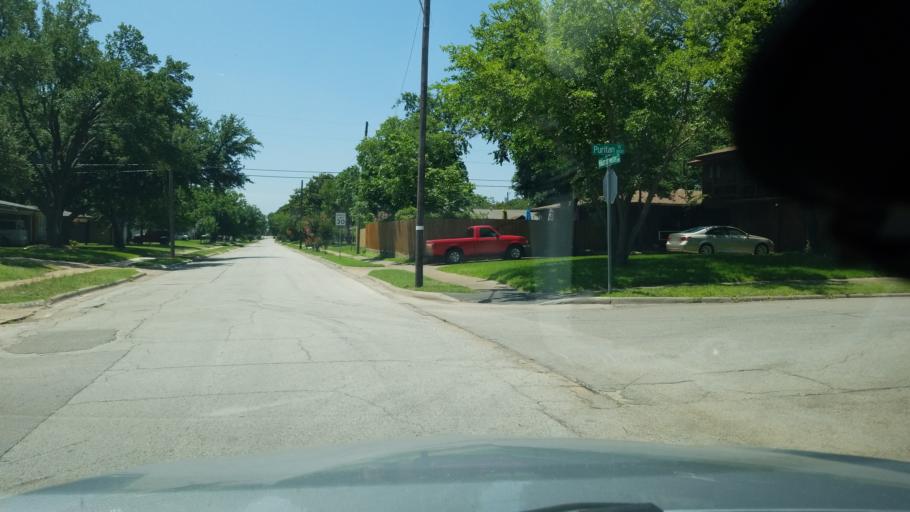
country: US
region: Texas
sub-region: Dallas County
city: Irving
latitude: 32.8364
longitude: -96.9683
